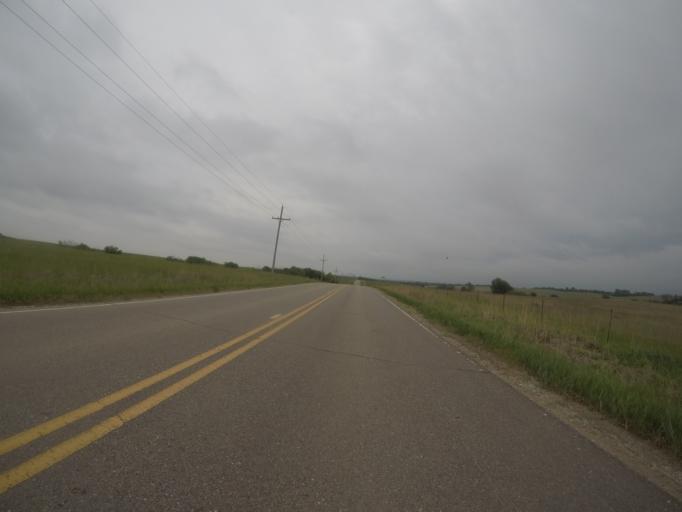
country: US
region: Kansas
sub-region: Pottawatomie County
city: Westmoreland
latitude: 39.5223
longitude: -96.2466
